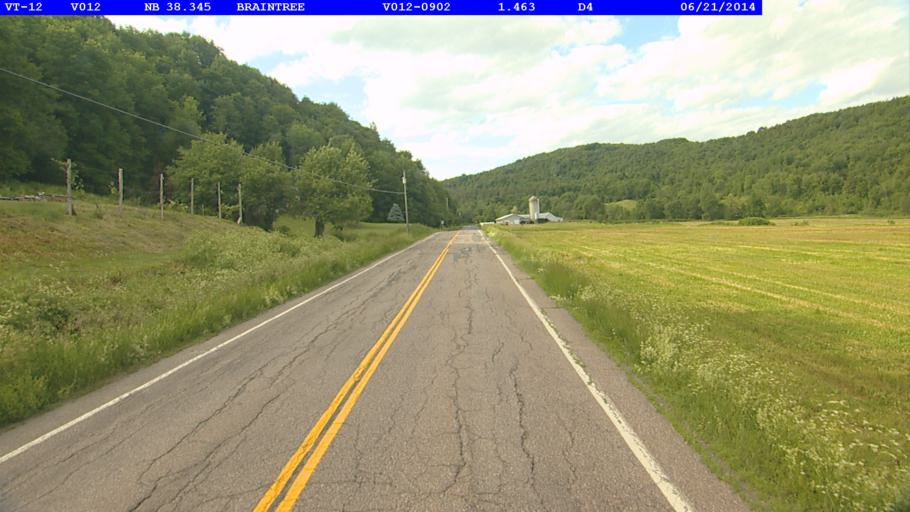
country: US
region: Vermont
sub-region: Orange County
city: Randolph
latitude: 44.0039
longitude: -72.6543
